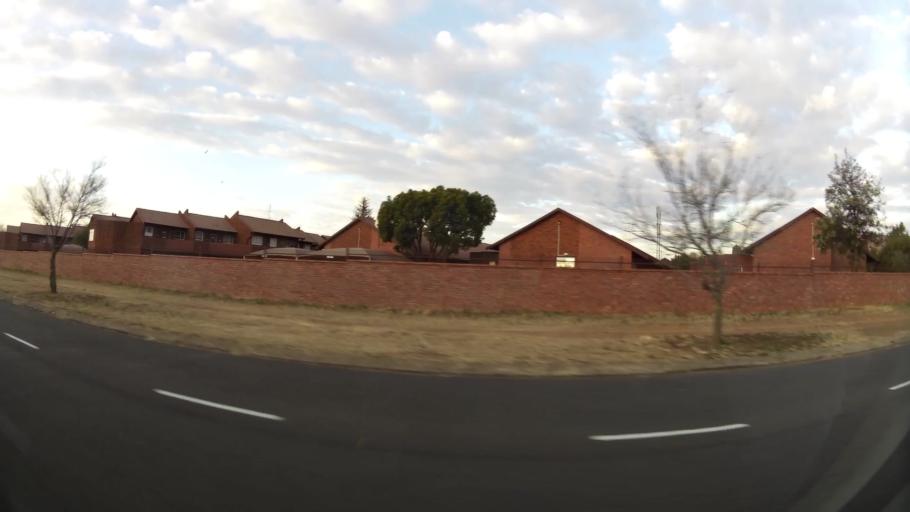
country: ZA
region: Orange Free State
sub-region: Mangaung Metropolitan Municipality
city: Bloemfontein
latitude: -29.1434
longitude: 26.1756
